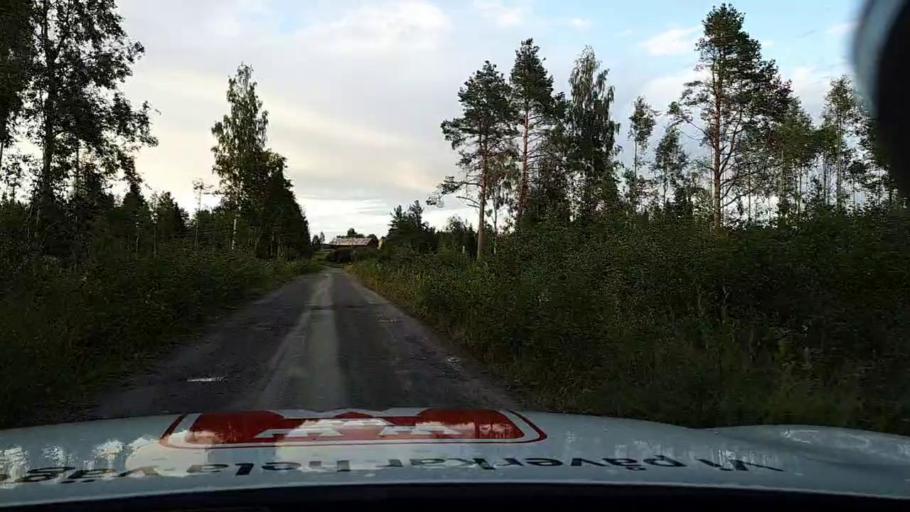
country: SE
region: Jaemtland
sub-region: Bergs Kommun
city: Hoverberg
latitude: 62.8689
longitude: 14.6197
